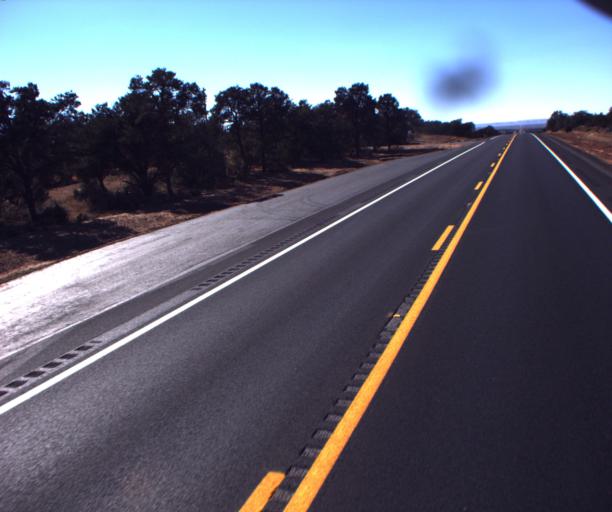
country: US
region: Arizona
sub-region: Apache County
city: Ganado
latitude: 35.7194
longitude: -109.3730
